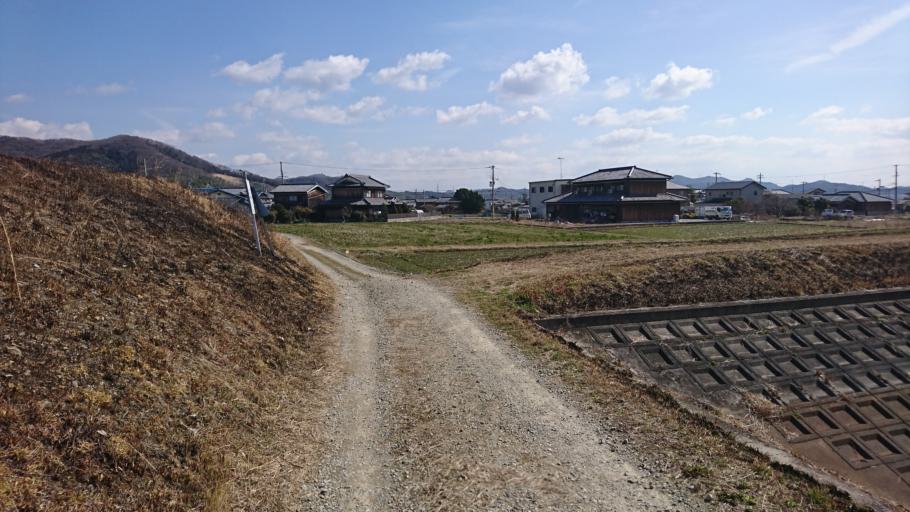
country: JP
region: Hyogo
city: Kakogawacho-honmachi
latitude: 34.8253
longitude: 134.8003
